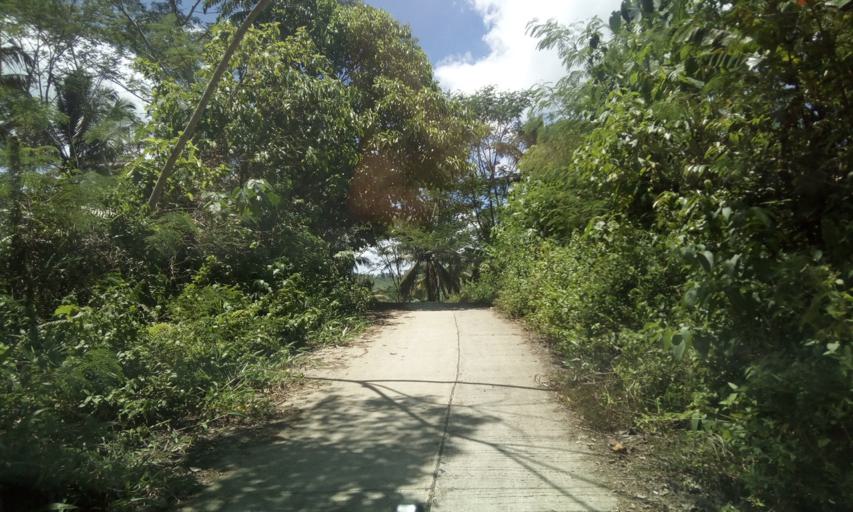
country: PH
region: Caraga
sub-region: Province of Agusan del Sur
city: Santa Josefa
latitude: 7.9541
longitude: 125.9892
